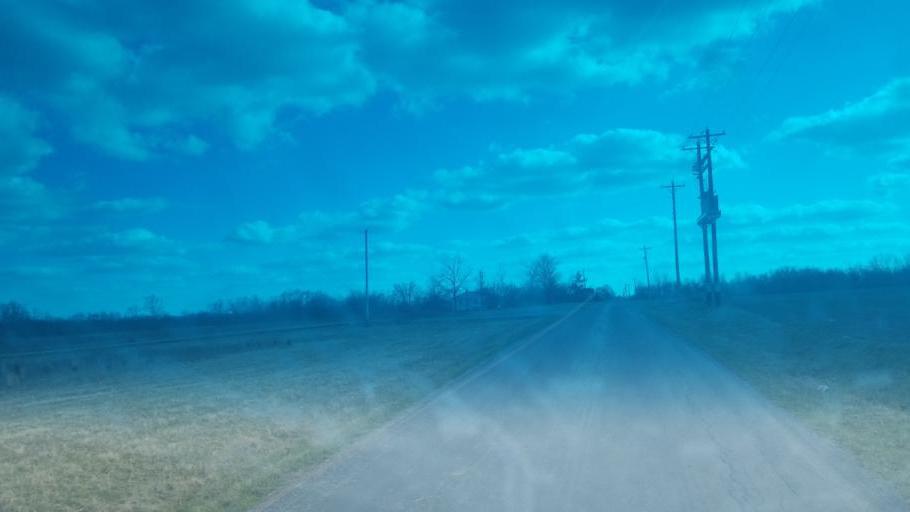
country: US
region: Ohio
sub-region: Highland County
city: Greenfield
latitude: 39.3453
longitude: -83.4188
